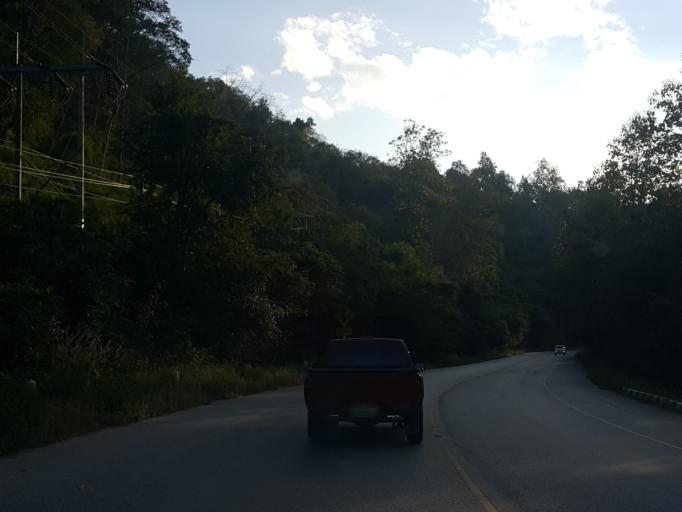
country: TH
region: Lampang
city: Chae Hom
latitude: 18.5069
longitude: 99.5553
